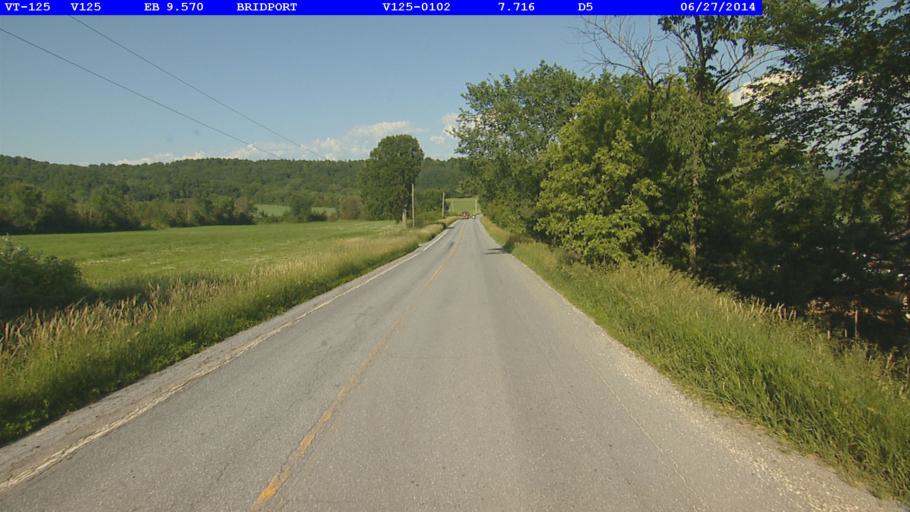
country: US
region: Vermont
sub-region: Addison County
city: Middlebury (village)
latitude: 43.9958
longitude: -73.2665
